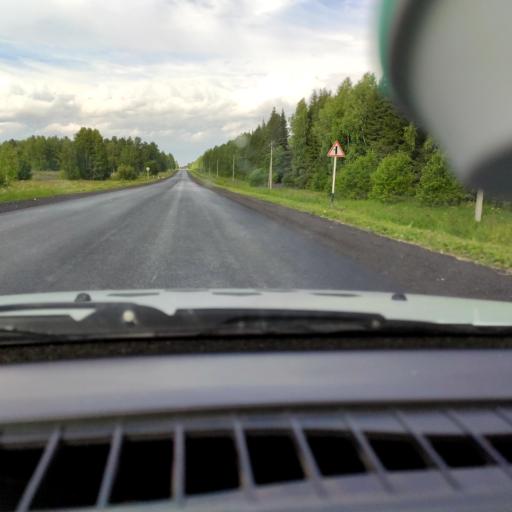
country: RU
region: Perm
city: Orda
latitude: 57.2247
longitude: 56.9576
